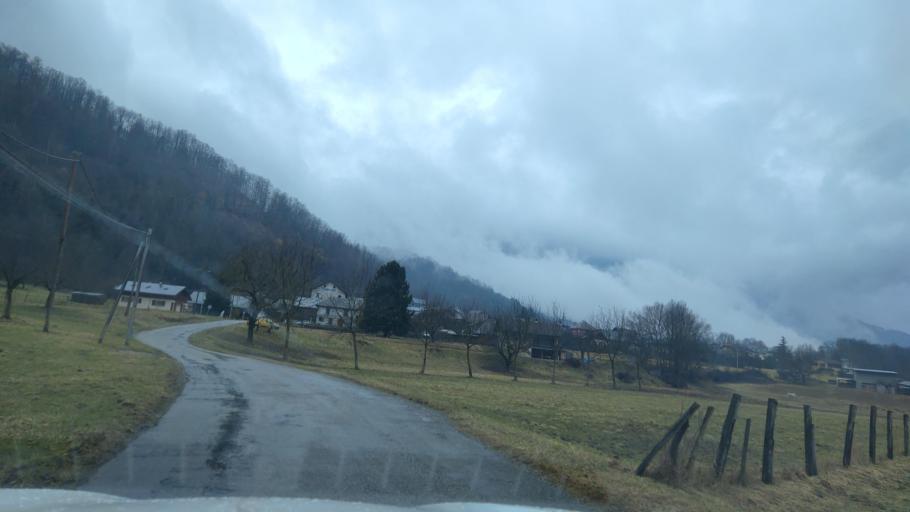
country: FR
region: Rhone-Alpes
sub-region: Departement de la Savoie
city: Saint-Remy-de-Maurienne
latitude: 45.4670
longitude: 6.2835
